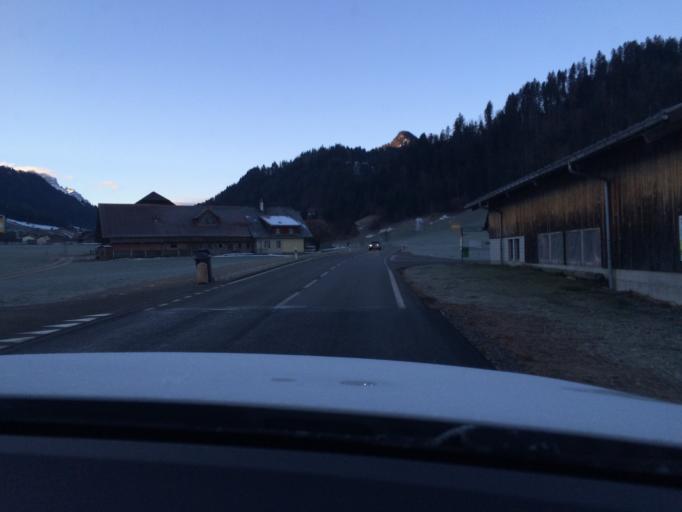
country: CH
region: Lucerne
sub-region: Entlebuch District
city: Escholzmatt
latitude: 46.8639
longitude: 7.9038
